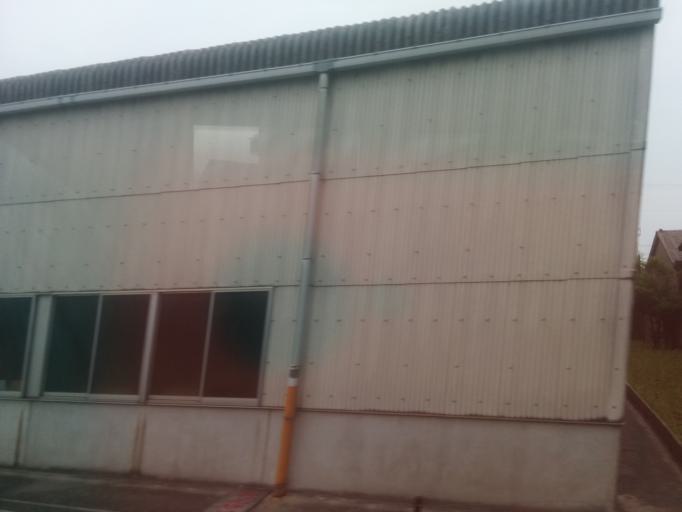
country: JP
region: Shiga Prefecture
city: Hikone
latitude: 35.2669
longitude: 136.2619
